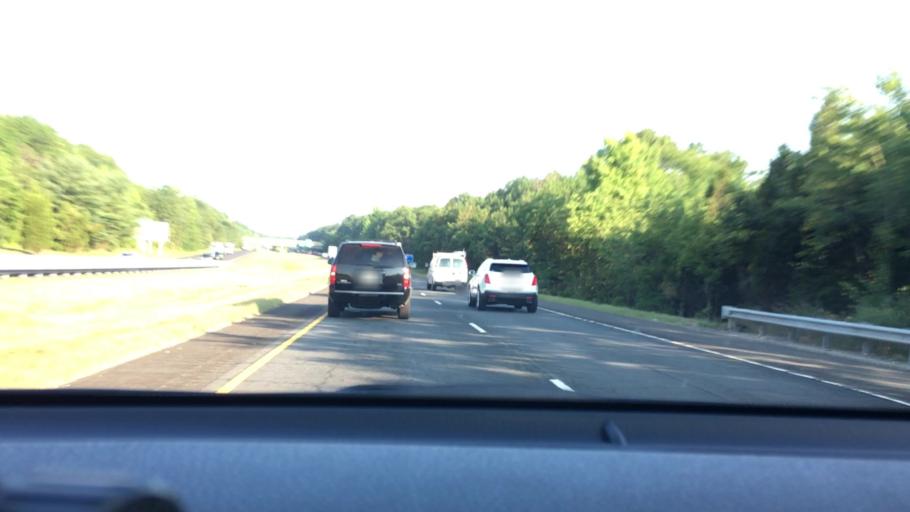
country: US
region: New Jersey
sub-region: Gloucester County
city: Clayton
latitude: 39.6441
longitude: -75.1029
